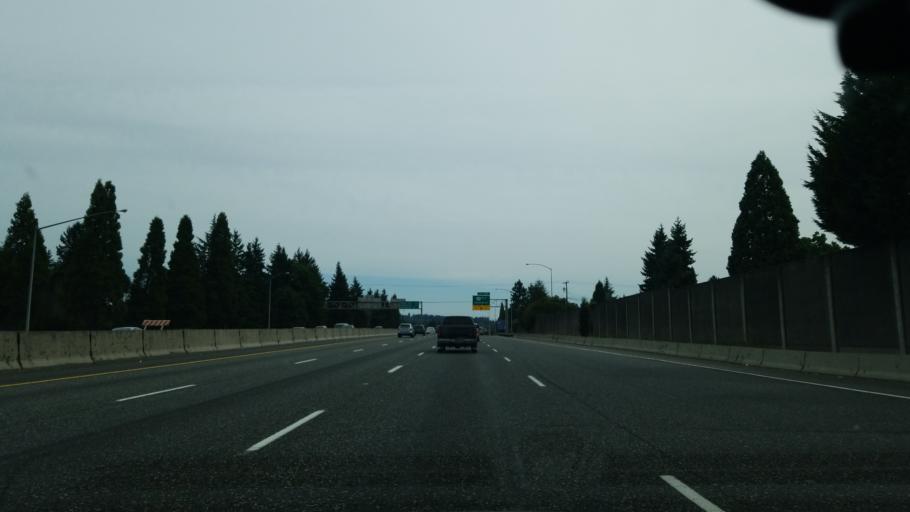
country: US
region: Oregon
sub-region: Clackamas County
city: Clackamas
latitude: 45.4148
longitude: -122.5740
